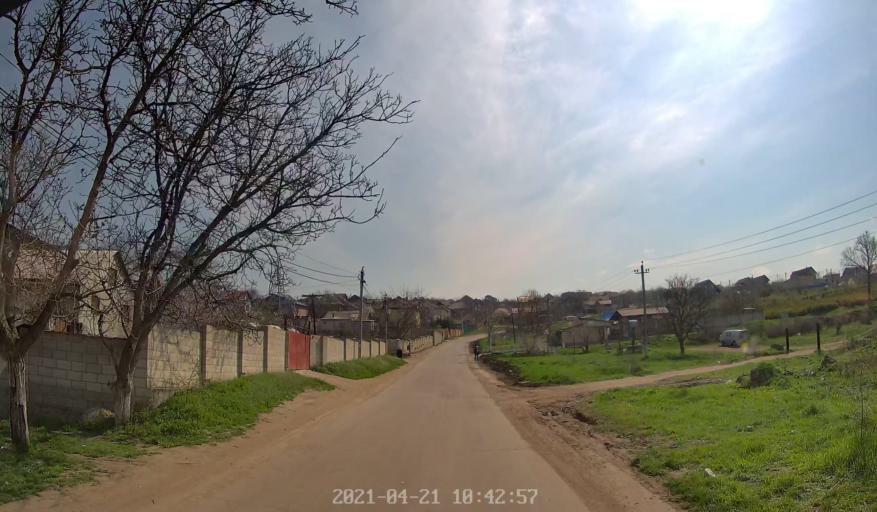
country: MD
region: Chisinau
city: Singera
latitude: 46.9784
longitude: 28.9416
